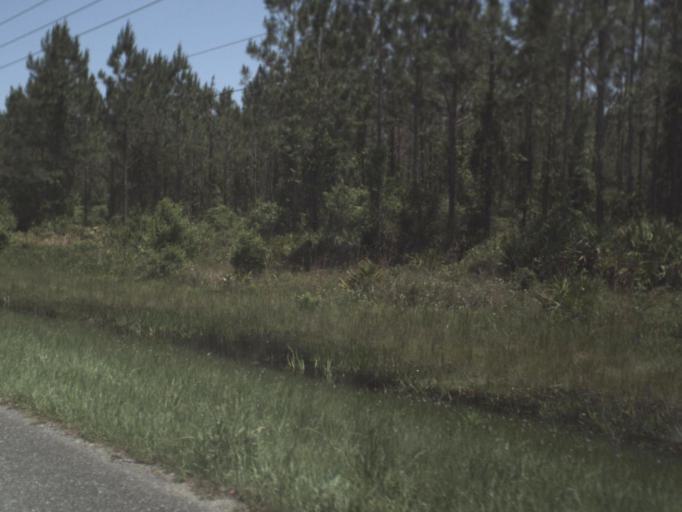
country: US
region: Florida
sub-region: Columbia County
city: Watertown
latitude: 30.1999
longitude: -82.4769
